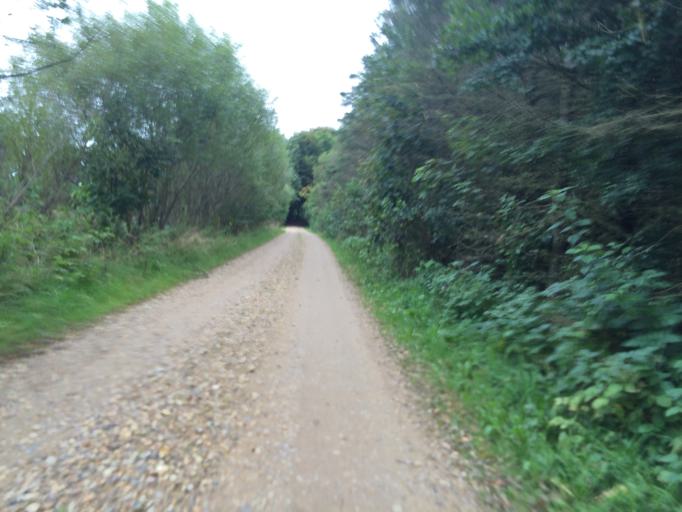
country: DK
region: Central Jutland
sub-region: Holstebro Kommune
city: Ulfborg
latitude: 56.2327
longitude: 8.4178
